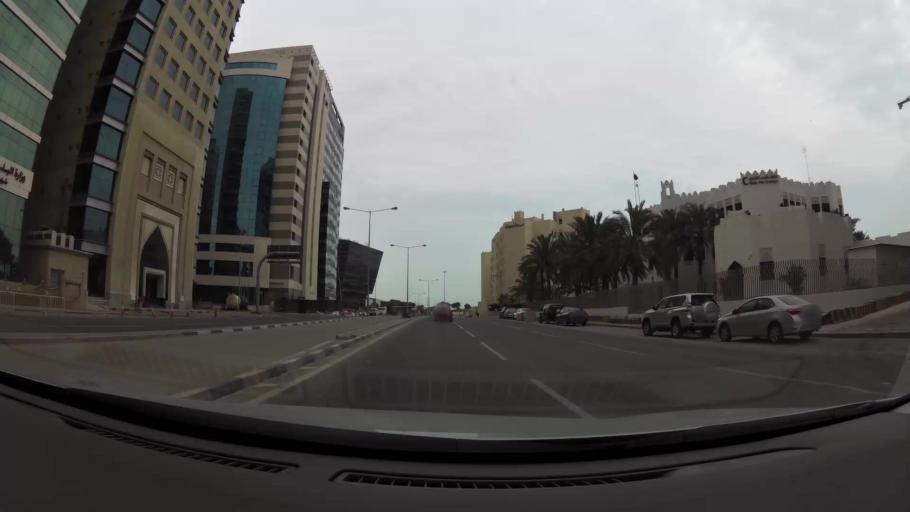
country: QA
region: Baladiyat ad Dawhah
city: Doha
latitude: 25.2889
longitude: 51.5442
